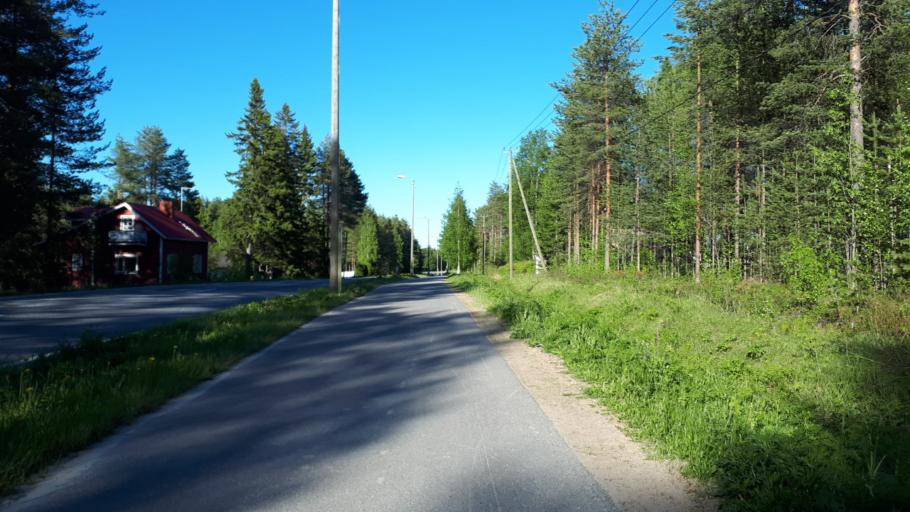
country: FI
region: Northern Ostrobothnia
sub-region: Oulunkaari
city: Ii
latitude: 65.3230
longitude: 25.4685
